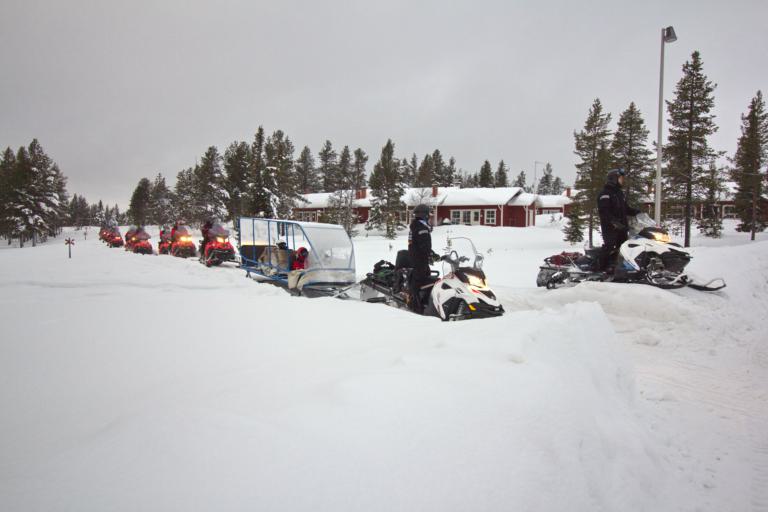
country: FI
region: Lapland
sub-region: Pohjois-Lappi
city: Ivalo
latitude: 68.4251
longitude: 27.4143
